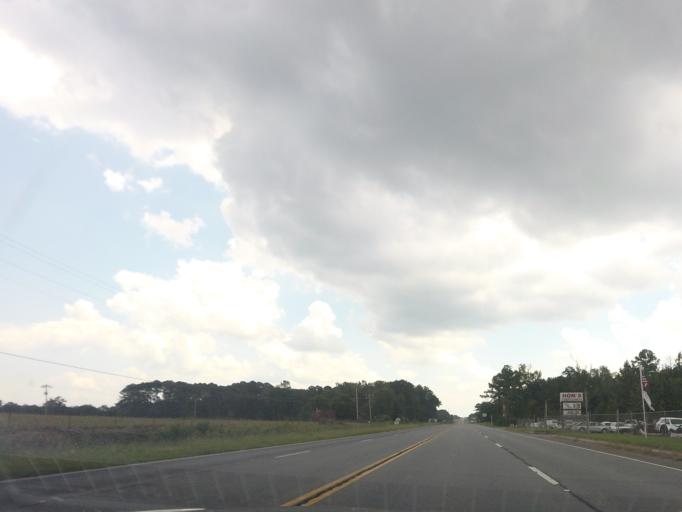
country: US
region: Georgia
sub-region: Bleckley County
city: Cochran
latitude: 32.4237
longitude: -83.3613
